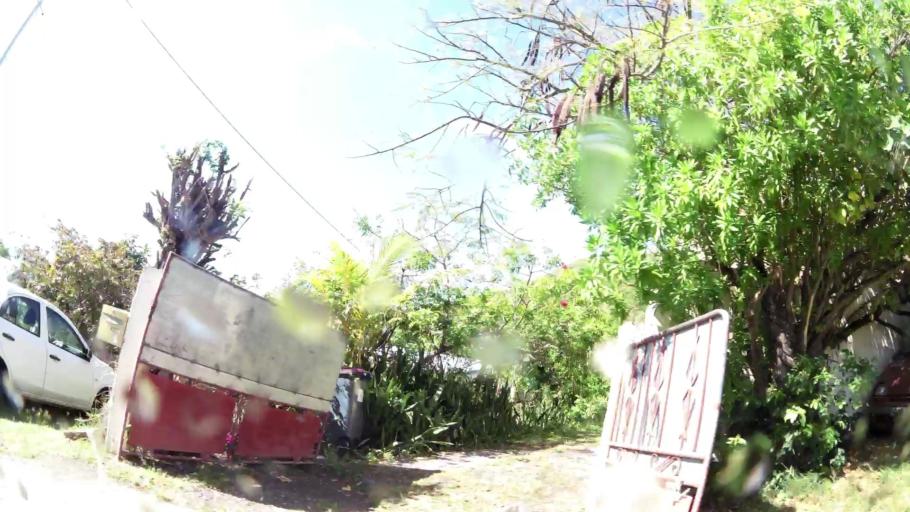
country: MQ
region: Martinique
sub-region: Martinique
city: Les Trois-Ilets
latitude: 14.4712
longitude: -61.0718
